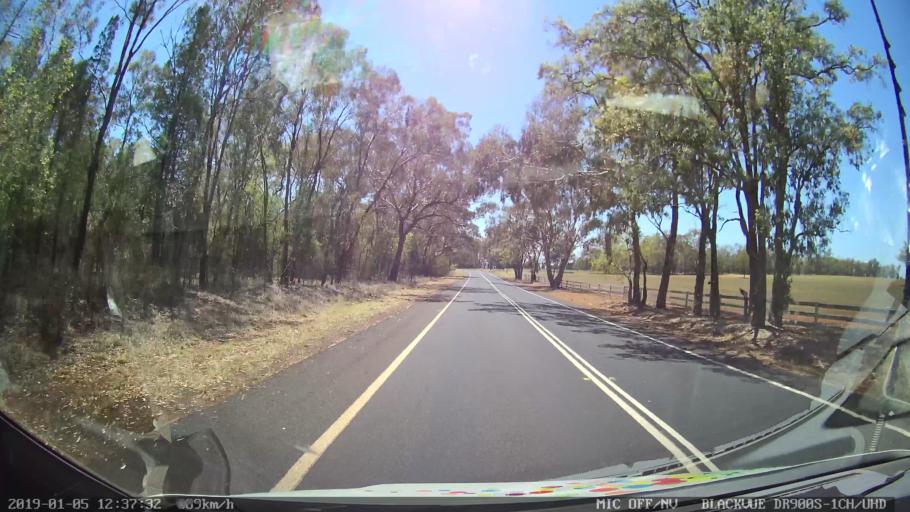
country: AU
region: New South Wales
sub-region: Warrumbungle Shire
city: Coonabarabran
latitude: -31.2028
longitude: 149.4561
